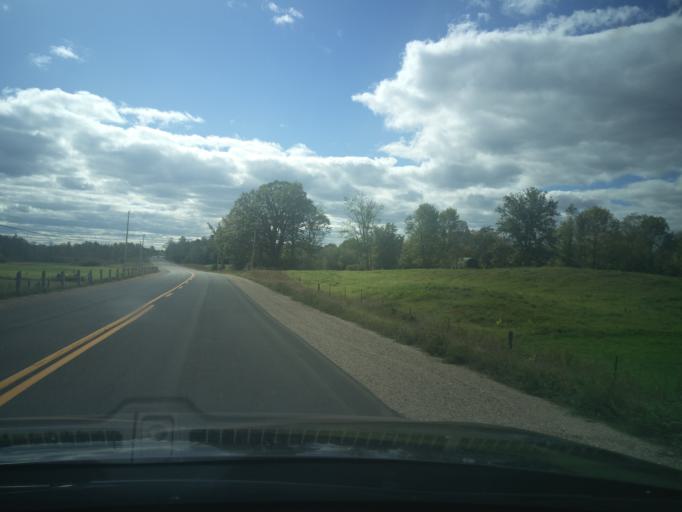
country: CA
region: Ontario
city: Perth
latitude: 44.7840
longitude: -76.3496
